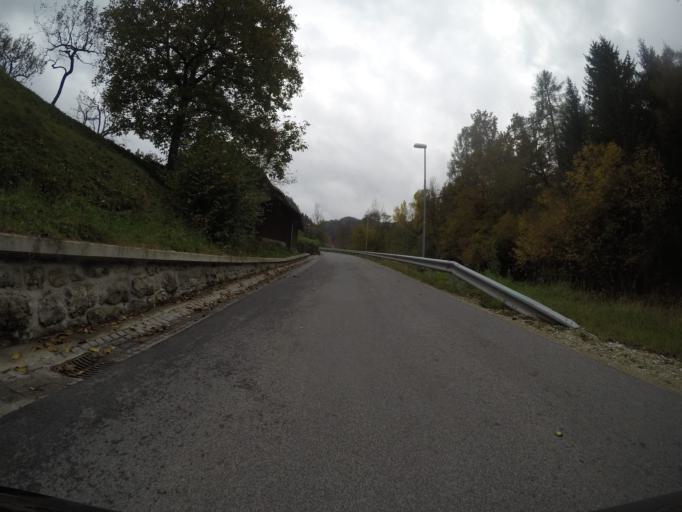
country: SI
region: Gorje
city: Zgornje Gorje
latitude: 46.3766
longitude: 14.0547
